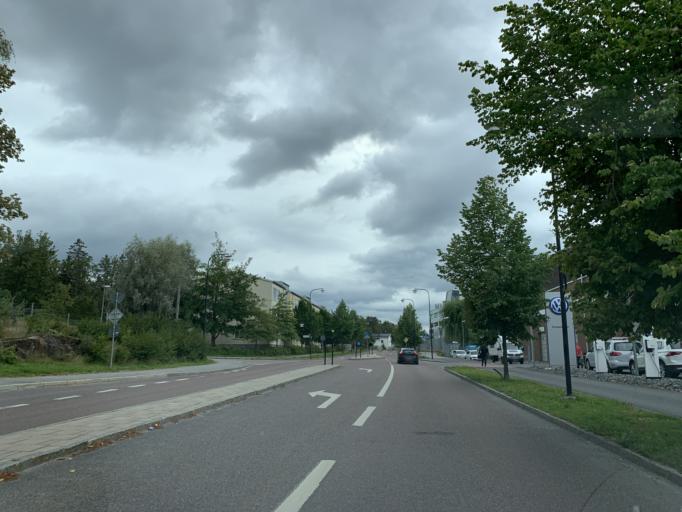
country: SE
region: Stockholm
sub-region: Huddinge Kommun
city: Segeltorp
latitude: 59.2803
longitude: 17.9236
